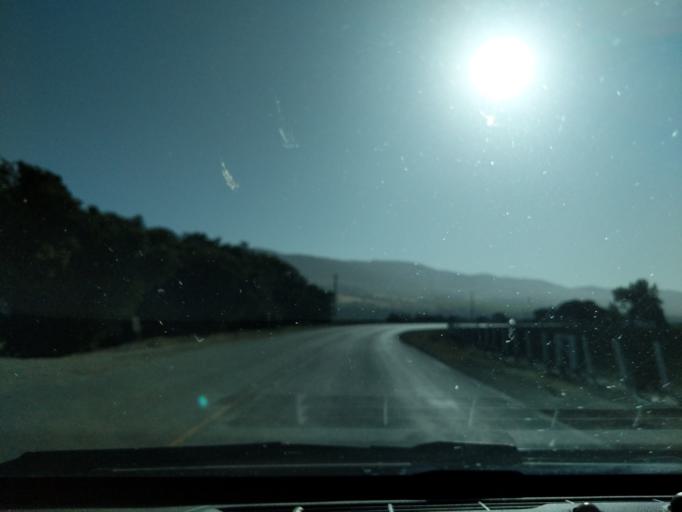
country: US
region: California
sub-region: Monterey County
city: Soledad
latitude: 36.4041
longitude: -121.3476
